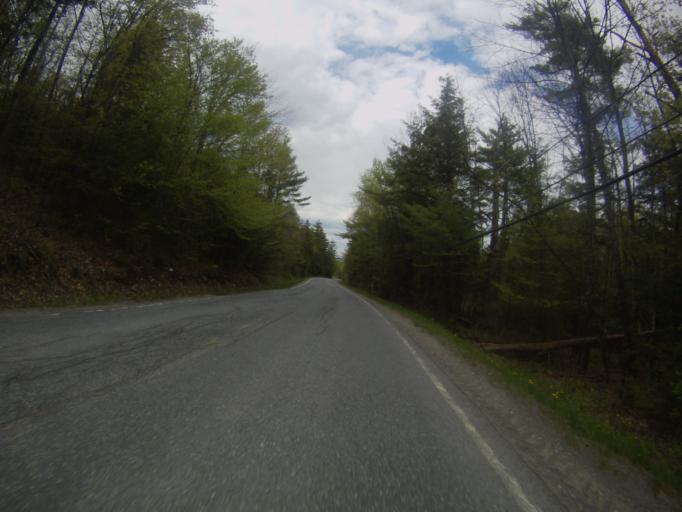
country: US
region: New York
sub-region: Essex County
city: Port Henry
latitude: 43.9917
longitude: -73.4917
